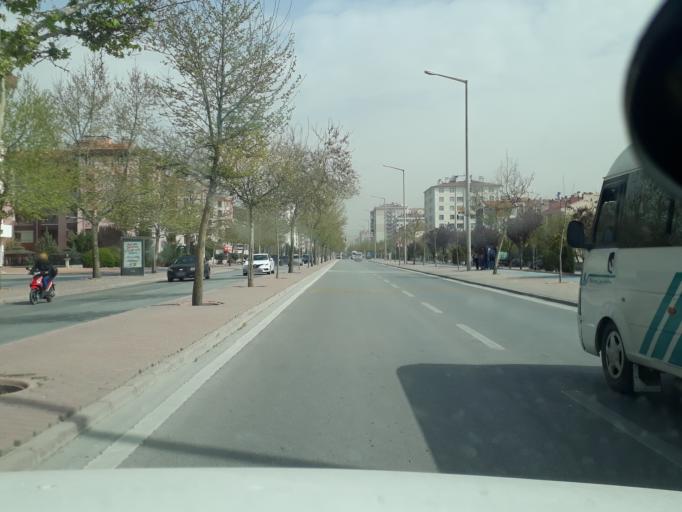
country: TR
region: Konya
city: Selcuklu
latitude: 37.9400
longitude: 32.4931
